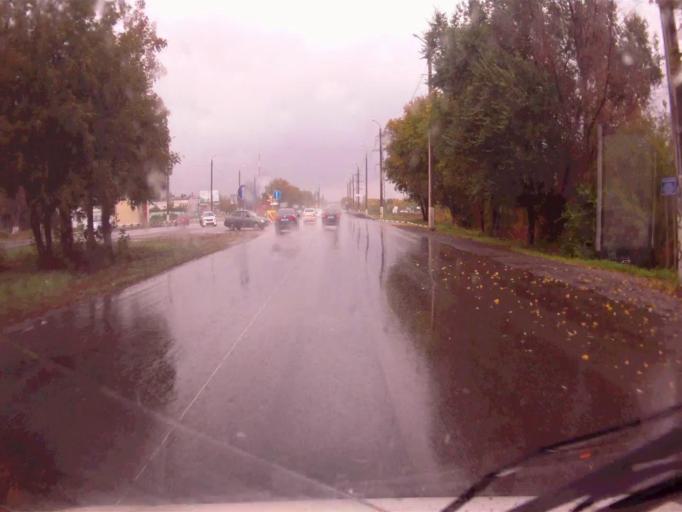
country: RU
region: Chelyabinsk
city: Dolgoderevenskoye
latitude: 55.2525
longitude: 61.3548
